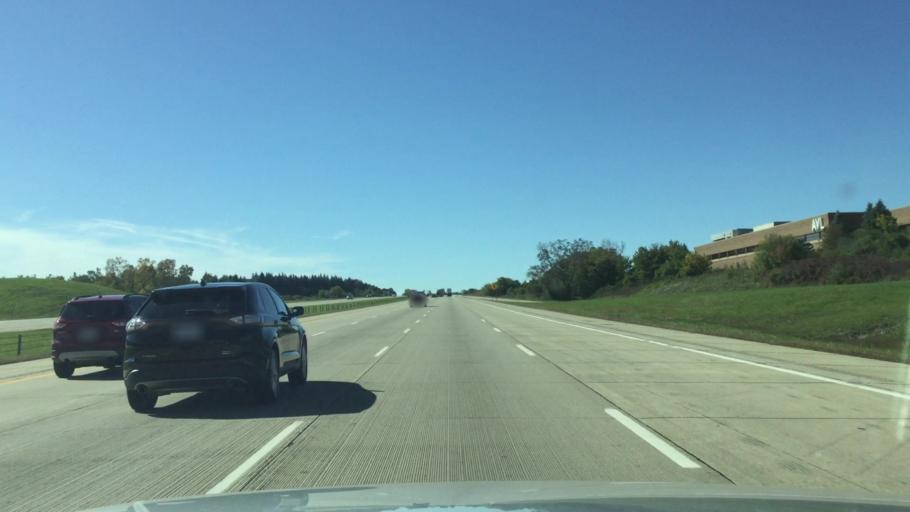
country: US
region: Michigan
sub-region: Wayne County
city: Plymouth
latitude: 42.3823
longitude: -83.5108
